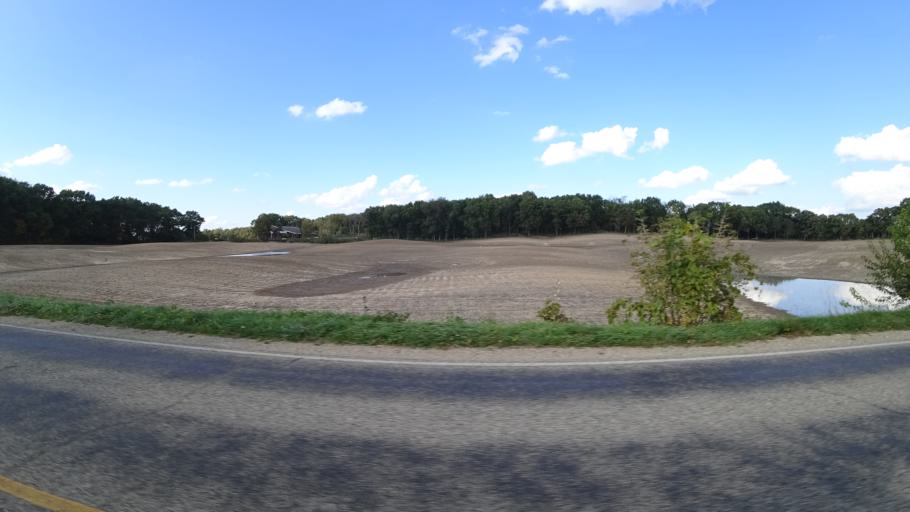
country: US
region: Michigan
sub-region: Saint Joseph County
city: Sturgis
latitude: 41.8537
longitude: -85.4804
